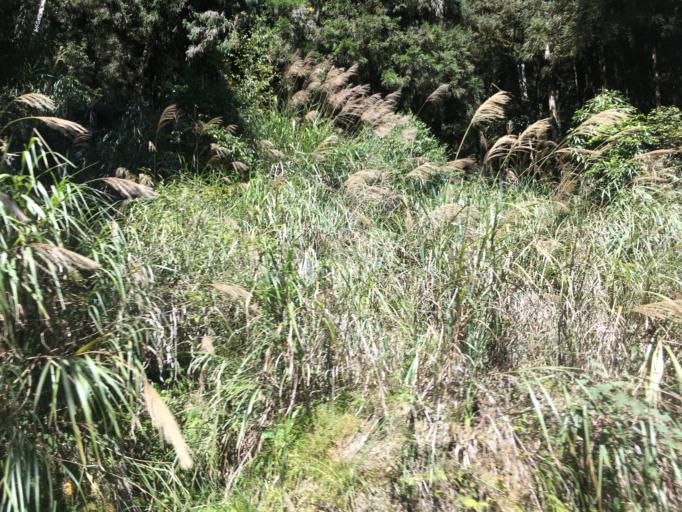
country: TW
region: Taiwan
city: Daxi
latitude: 24.5813
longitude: 121.4117
